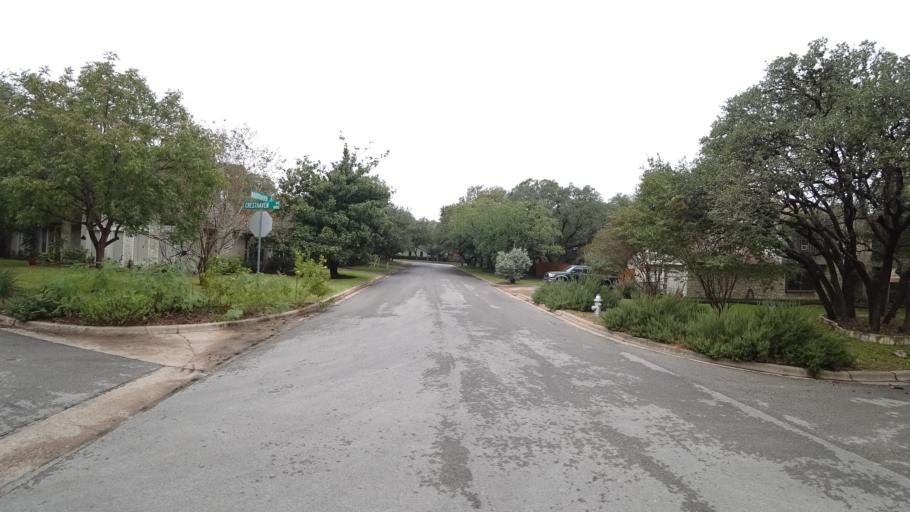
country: US
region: Texas
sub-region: Travis County
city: Rollingwood
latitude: 30.2590
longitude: -97.7819
